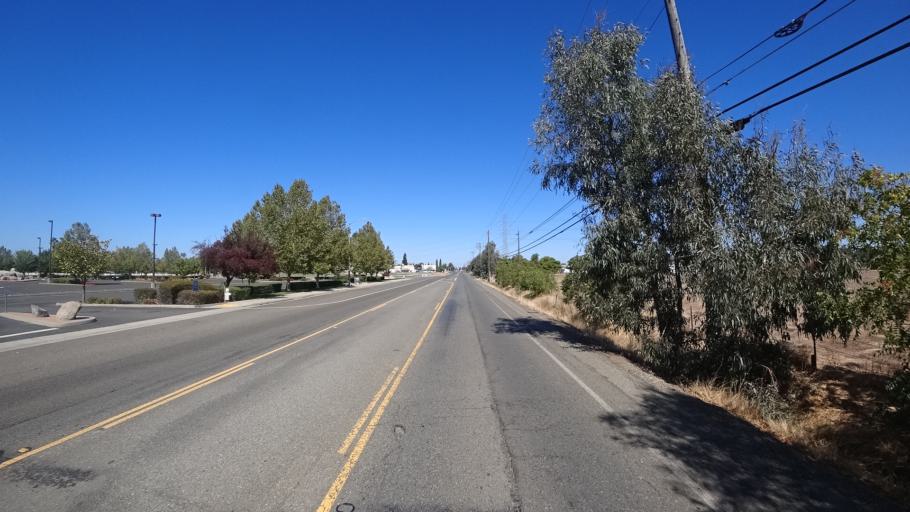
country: US
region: California
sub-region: Sacramento County
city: Vineyard
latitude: 38.4481
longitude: -121.3347
